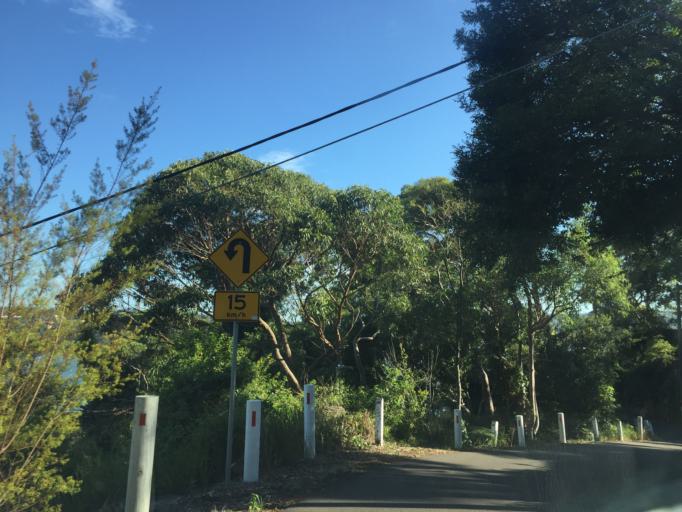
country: AU
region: New South Wales
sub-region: Pittwater
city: North Narrabeen
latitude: -33.7076
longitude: 151.2822
